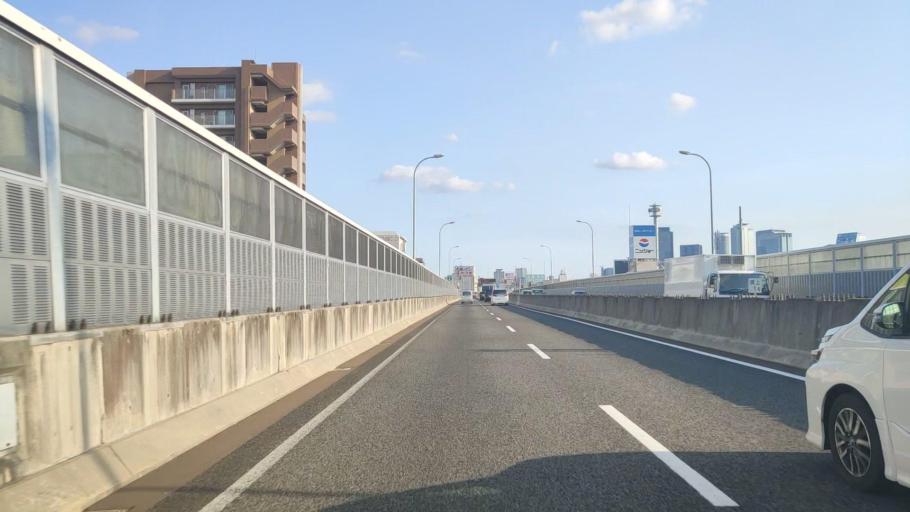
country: JP
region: Aichi
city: Nagoya-shi
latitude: 35.1914
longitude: 136.8910
